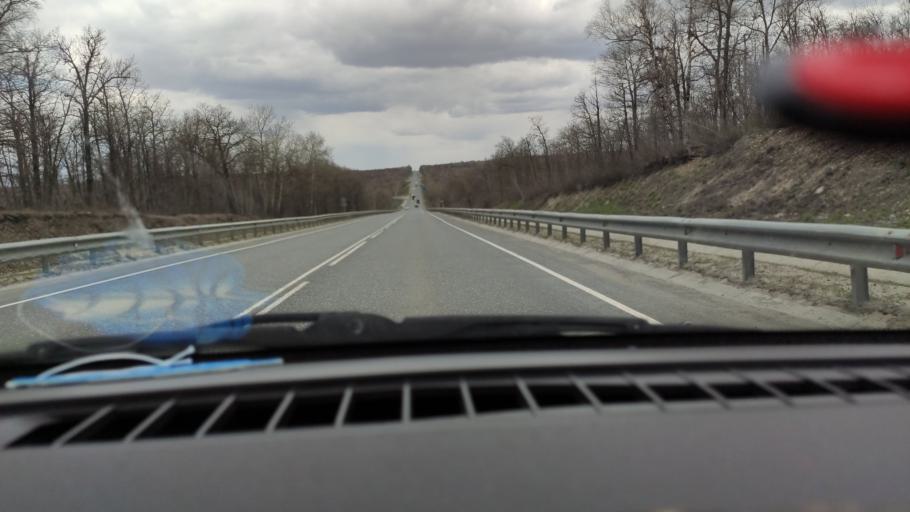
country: RU
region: Saratov
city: Vol'sk
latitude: 52.1088
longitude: 47.3840
